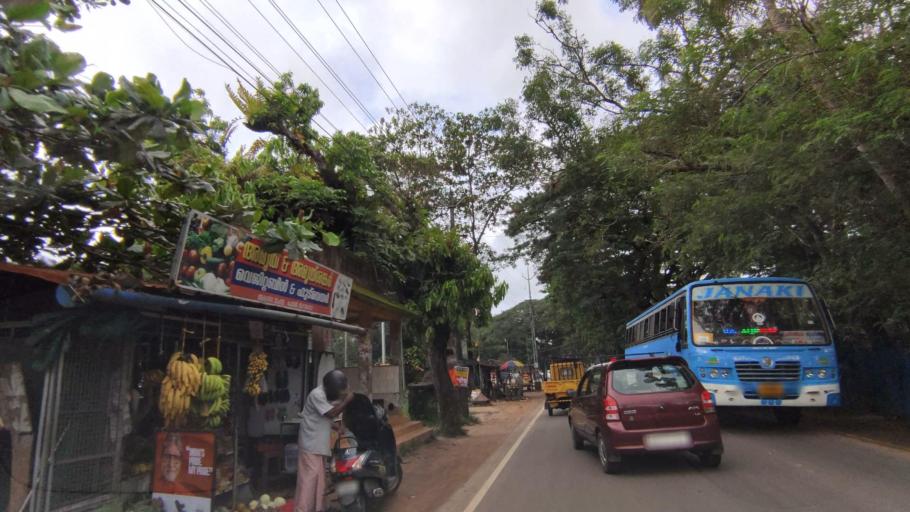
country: IN
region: Kerala
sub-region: Alappuzha
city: Shertallai
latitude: 9.6147
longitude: 76.3633
